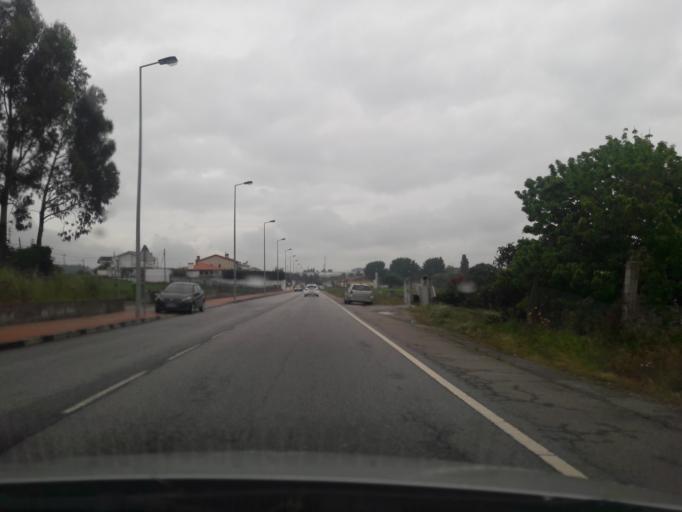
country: PT
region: Porto
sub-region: Vila do Conde
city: Arvore
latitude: 41.3382
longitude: -8.7280
